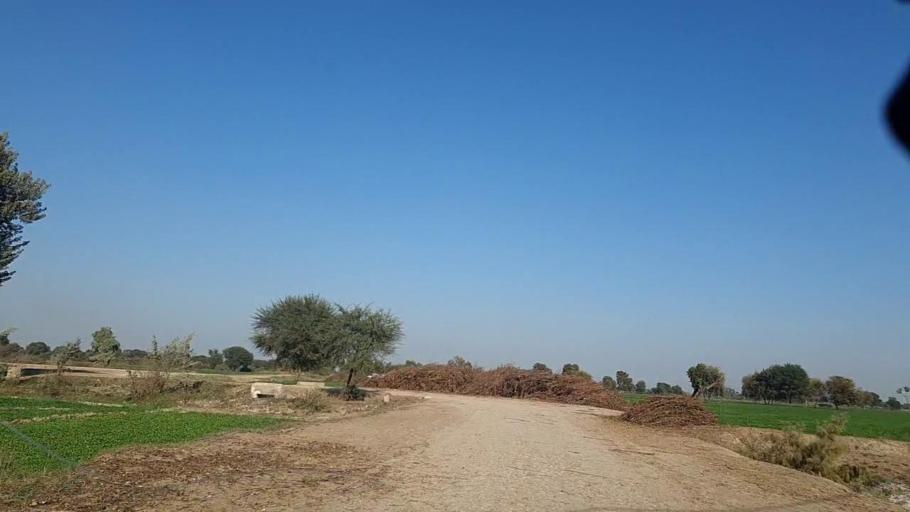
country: PK
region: Sindh
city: Khanpur
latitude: 27.7802
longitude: 69.3554
